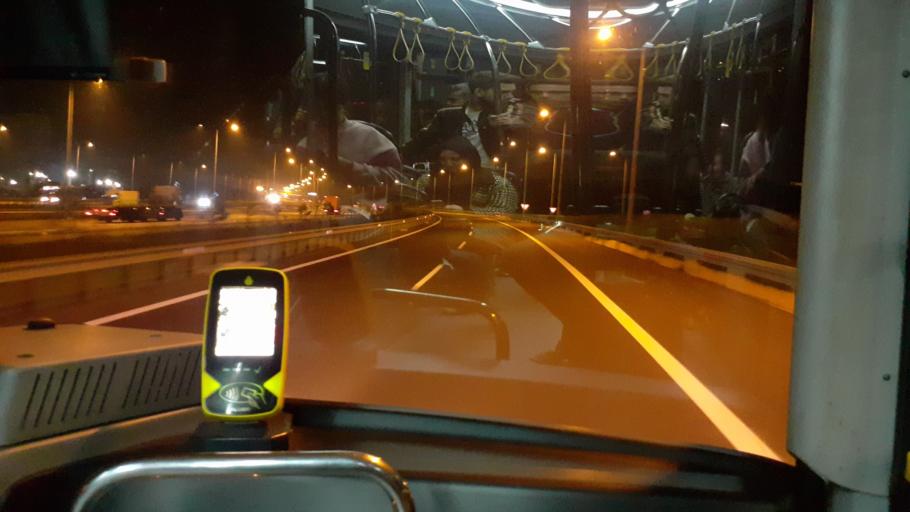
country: TR
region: Istanbul
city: Durusu
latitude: 41.2370
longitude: 28.7917
